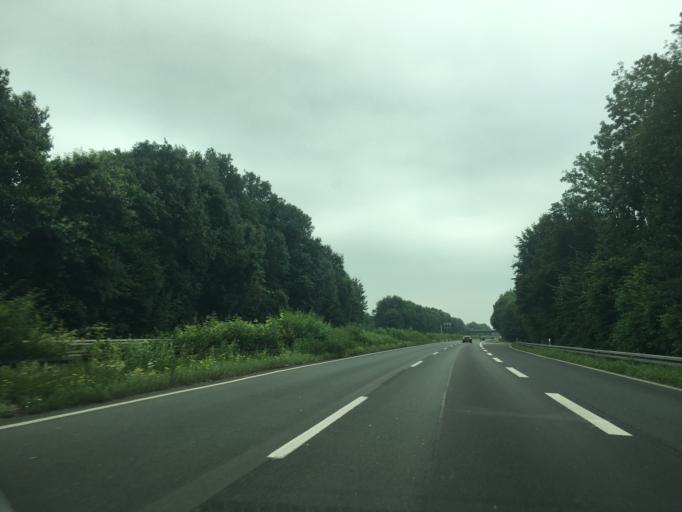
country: DE
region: North Rhine-Westphalia
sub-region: Regierungsbezirk Munster
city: Recklinghausen
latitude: 51.6414
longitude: 7.1714
